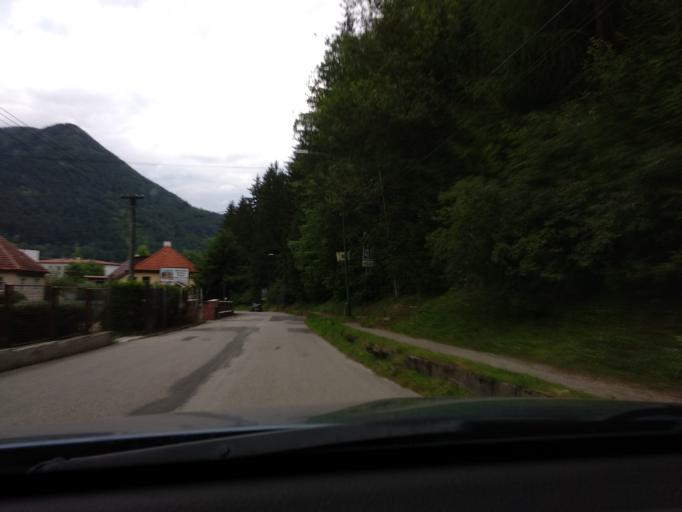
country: SK
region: Zilinsky
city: Ruzomberok
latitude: 49.0792
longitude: 19.2791
